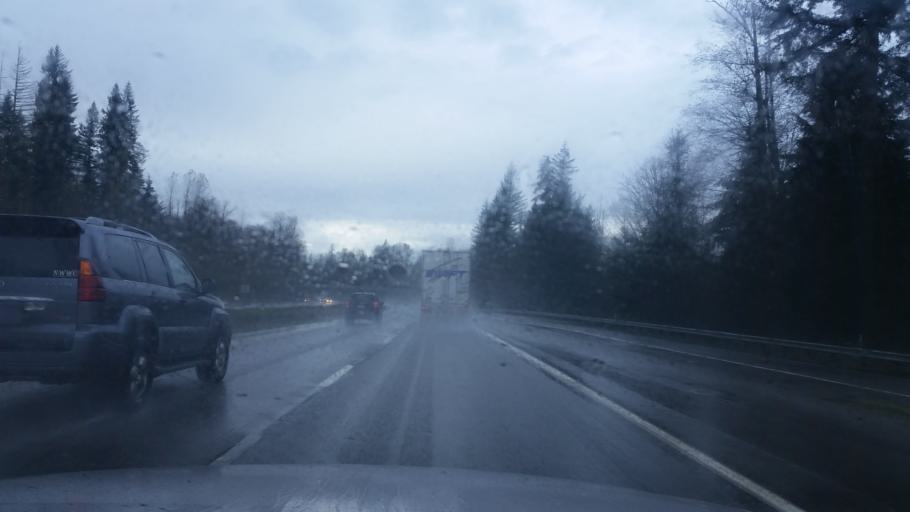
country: US
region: Washington
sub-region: King County
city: Hobart
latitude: 47.4345
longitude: -121.9795
